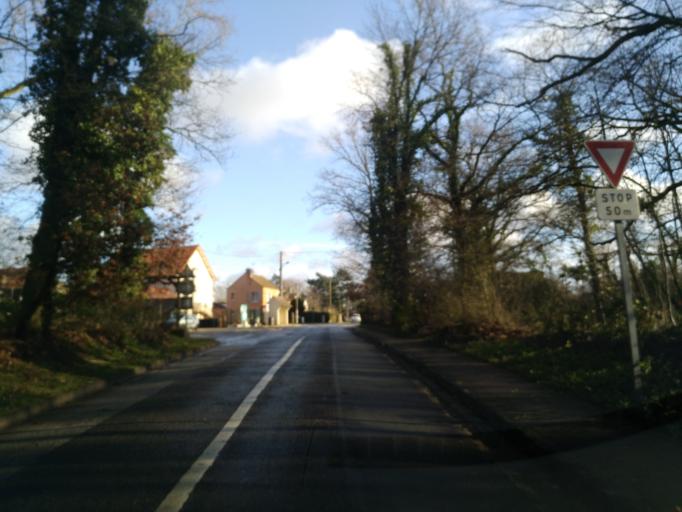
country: FR
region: Ile-de-France
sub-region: Departement des Yvelines
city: Neauphle-le-Chateau
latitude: 48.8218
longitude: 1.9005
